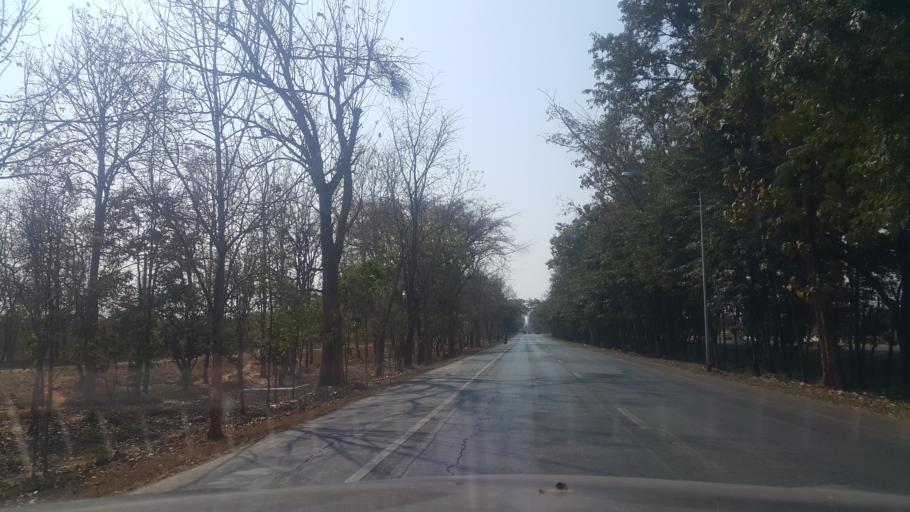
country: TH
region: Nakhon Ratchasima
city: Nakhon Ratchasima
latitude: 14.8813
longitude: 102.0718
